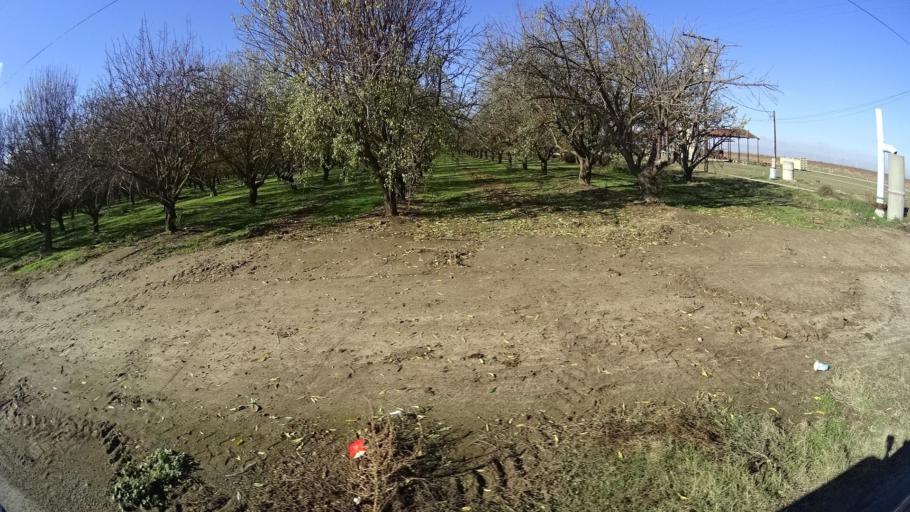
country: US
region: California
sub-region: Kern County
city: Delano
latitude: 35.7249
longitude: -119.2585
